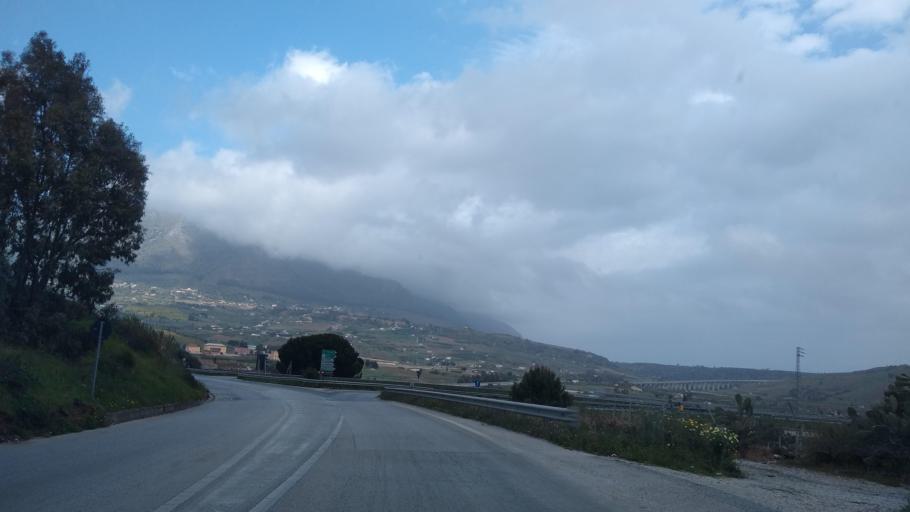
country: IT
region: Sicily
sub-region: Trapani
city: Alcamo
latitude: 37.9722
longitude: 12.9278
